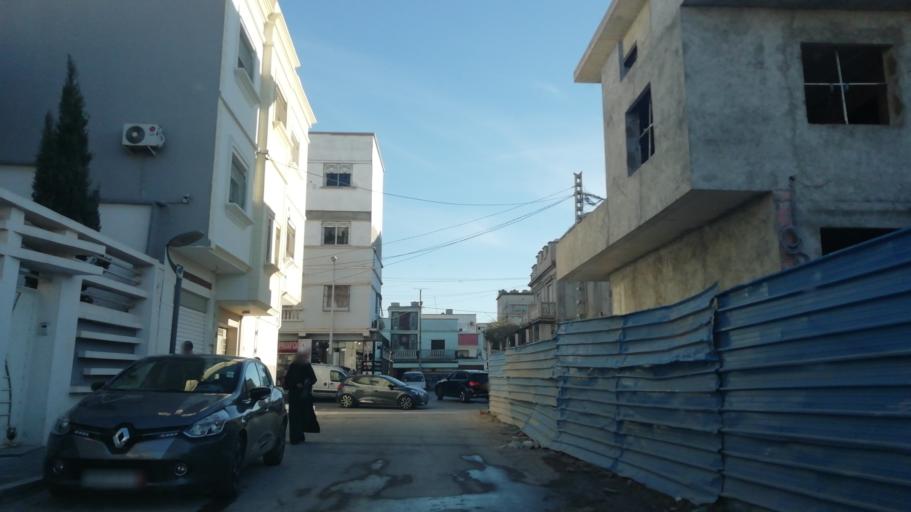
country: DZ
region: Oran
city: Oran
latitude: 35.7079
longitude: -0.6061
